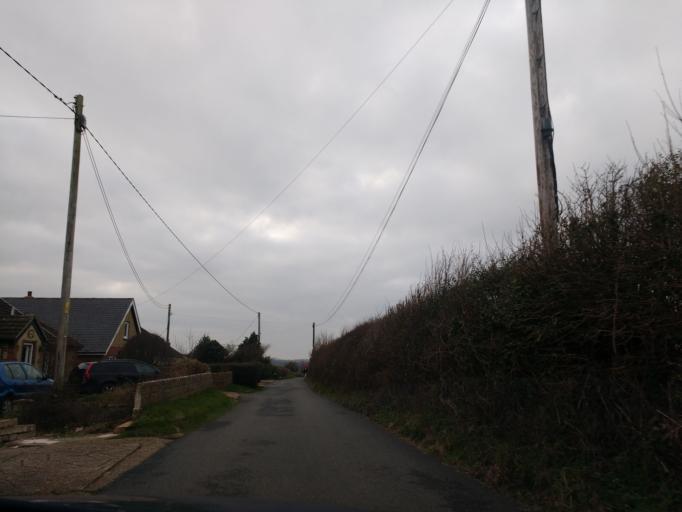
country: GB
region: England
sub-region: Isle of Wight
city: Shalfleet
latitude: 50.6879
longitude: -1.3954
